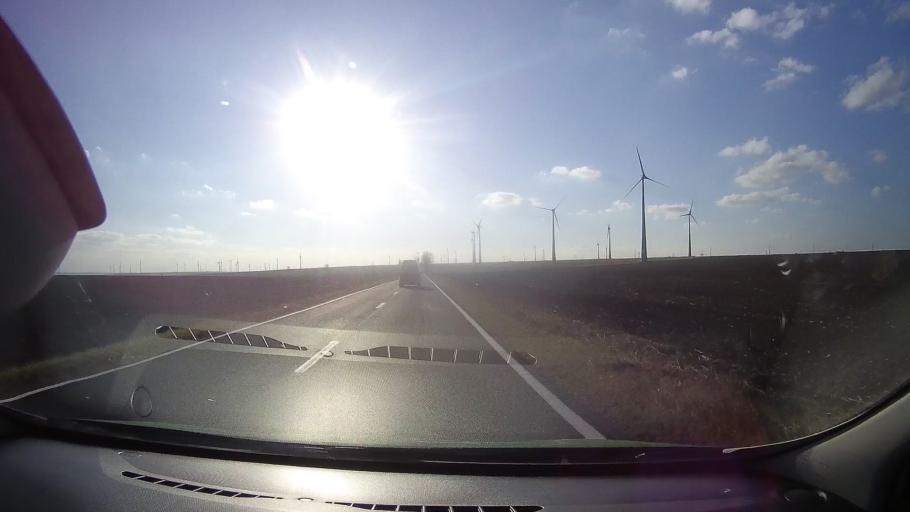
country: RO
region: Tulcea
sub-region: Comuna Topolog
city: Topolog
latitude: 44.8298
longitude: 28.2821
